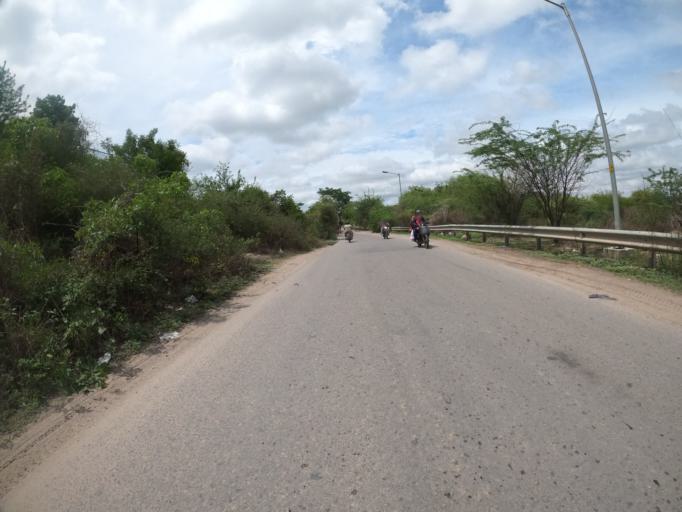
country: IN
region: Telangana
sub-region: Hyderabad
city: Hyderabad
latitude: 17.3160
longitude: 78.3720
